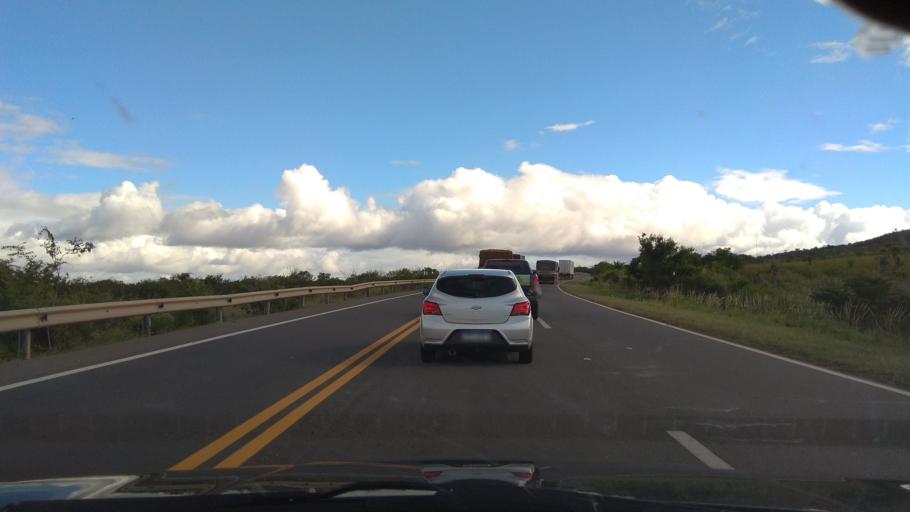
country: BR
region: Bahia
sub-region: Castro Alves
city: Castro Alves
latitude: -12.6492
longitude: -39.6068
